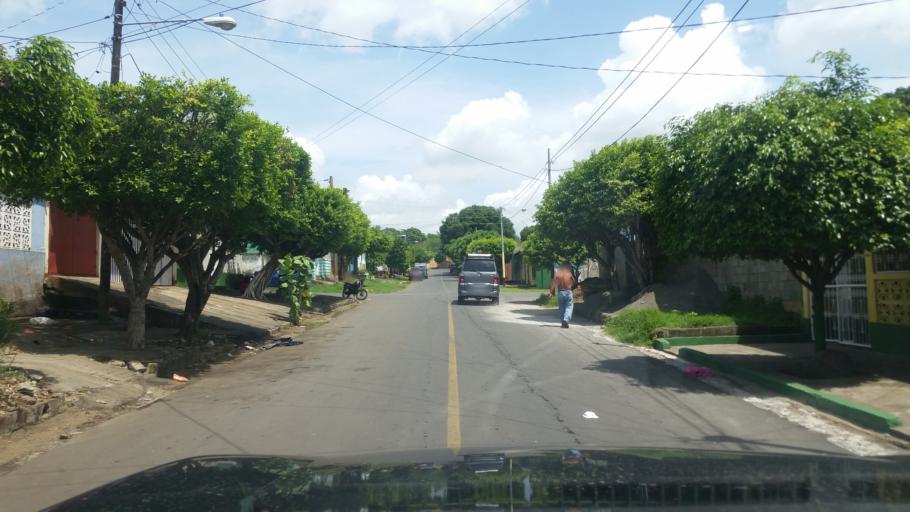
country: NI
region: Managua
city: Managua
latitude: 12.1141
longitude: -86.2334
